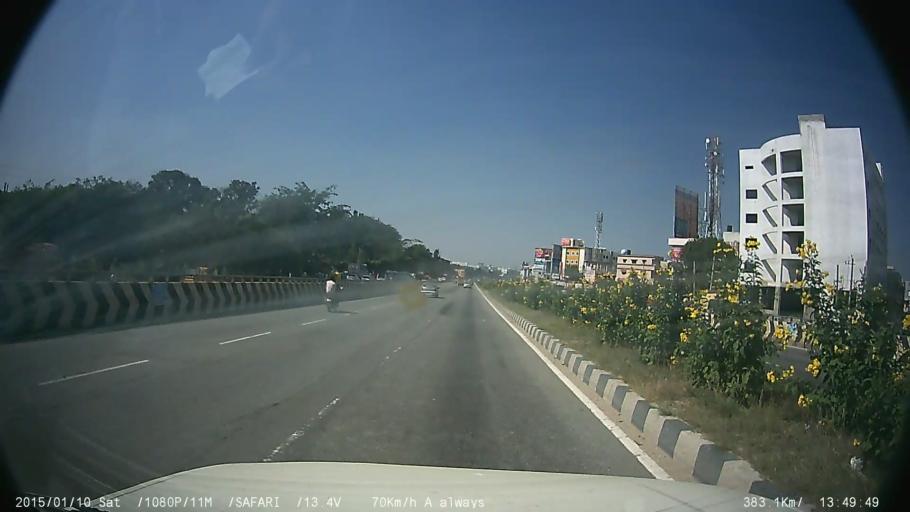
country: IN
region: Karnataka
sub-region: Bangalore Urban
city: Anekal
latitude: 12.8209
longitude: 77.6872
